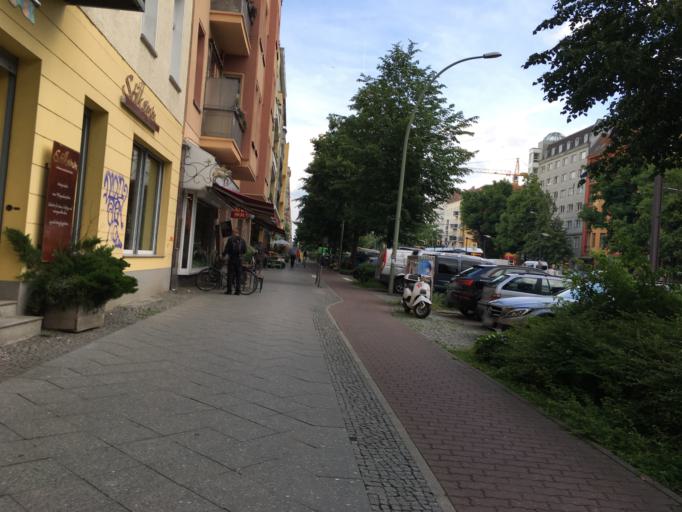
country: DE
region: Berlin
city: Prenzlauer Berg Bezirk
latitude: 52.5345
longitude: 13.4211
